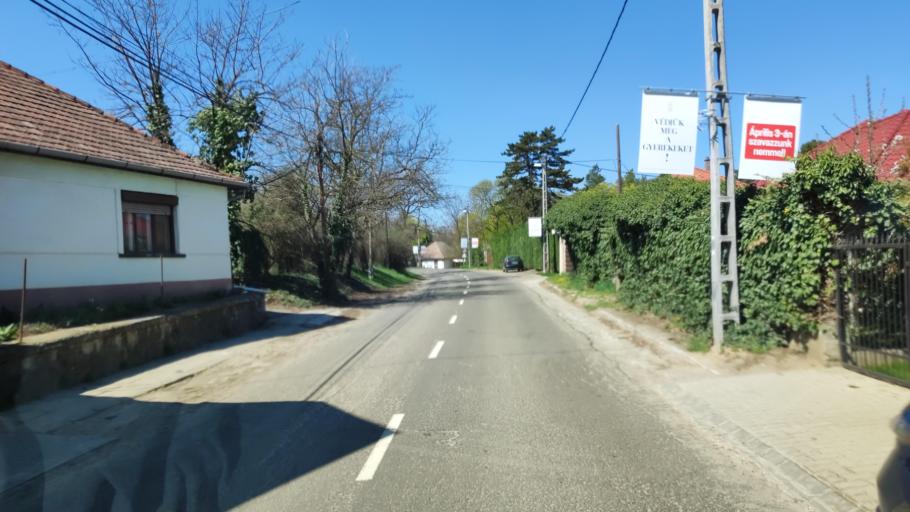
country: HU
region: Pest
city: Kosd
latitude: 47.7997
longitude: 19.1786
